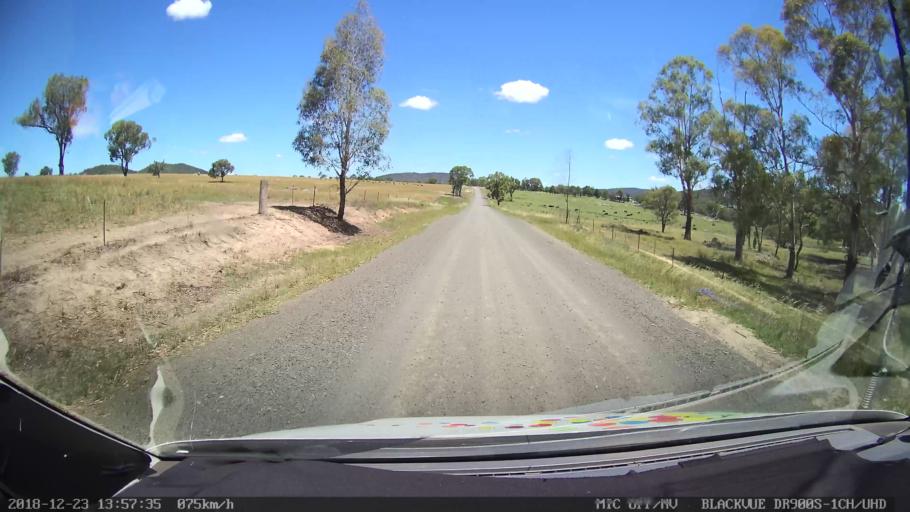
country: AU
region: New South Wales
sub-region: Tamworth Municipality
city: Manilla
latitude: -30.5894
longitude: 151.0936
